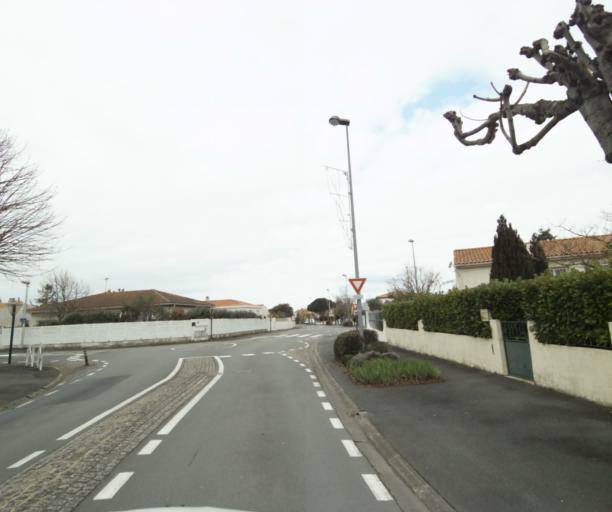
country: FR
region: Poitou-Charentes
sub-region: Departement de la Charente-Maritime
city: Lagord
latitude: 46.1863
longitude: -1.1529
